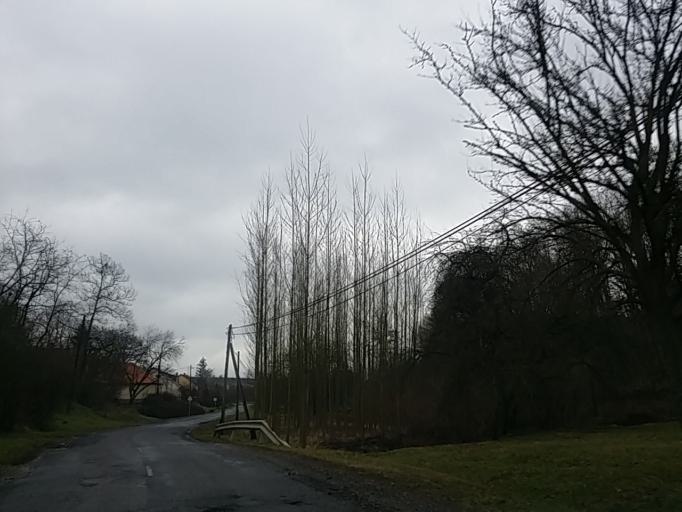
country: HU
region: Borsod-Abauj-Zemplen
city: Saly
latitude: 47.9506
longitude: 20.6240
